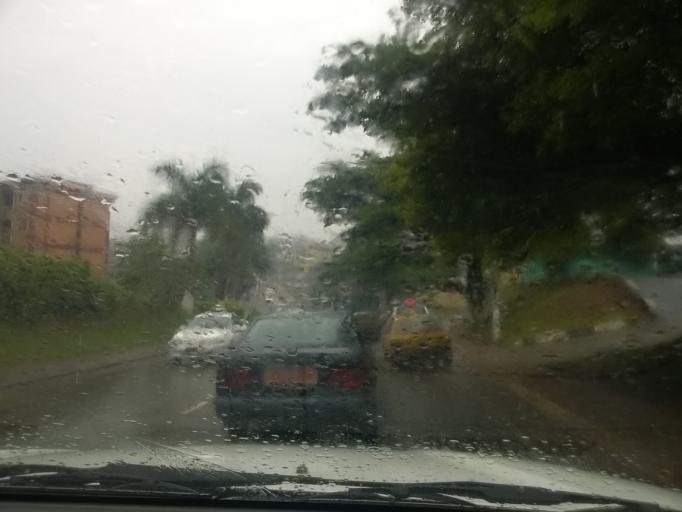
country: CM
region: Centre
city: Yaounde
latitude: 3.8863
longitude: 11.5066
